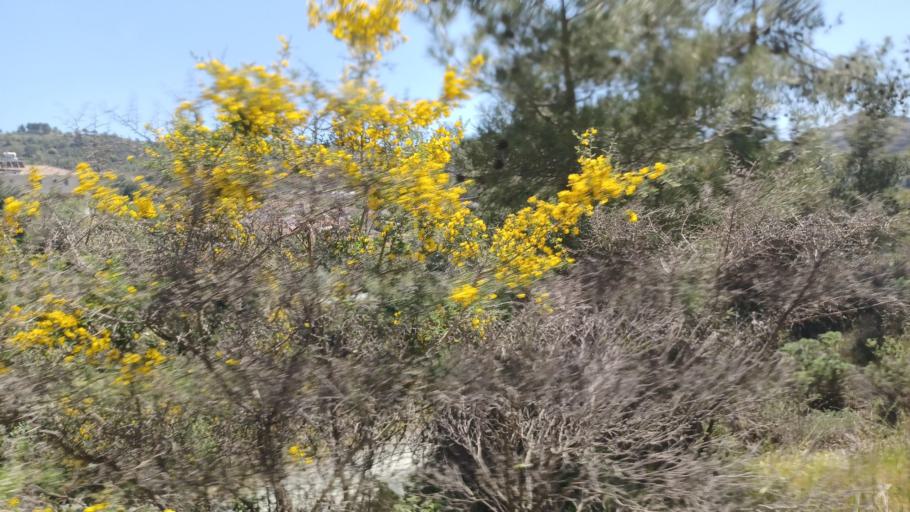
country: CY
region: Limassol
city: Parekklisha
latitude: 34.8147
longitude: 33.1426
